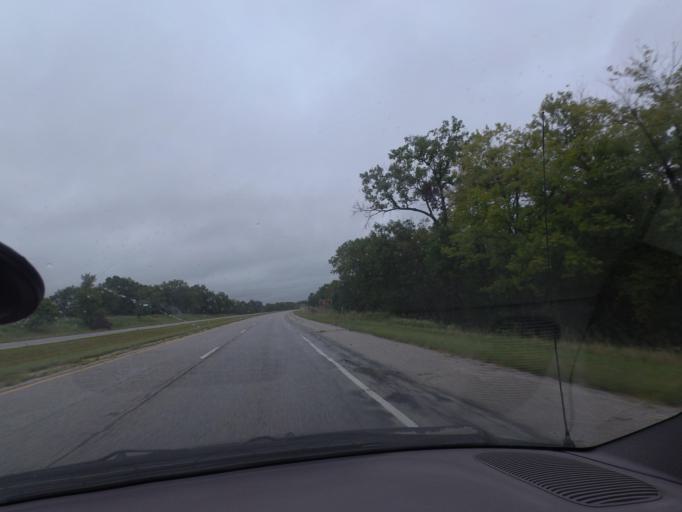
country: US
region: Illinois
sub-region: Pike County
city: Griggsville
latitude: 39.6734
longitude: -90.7824
